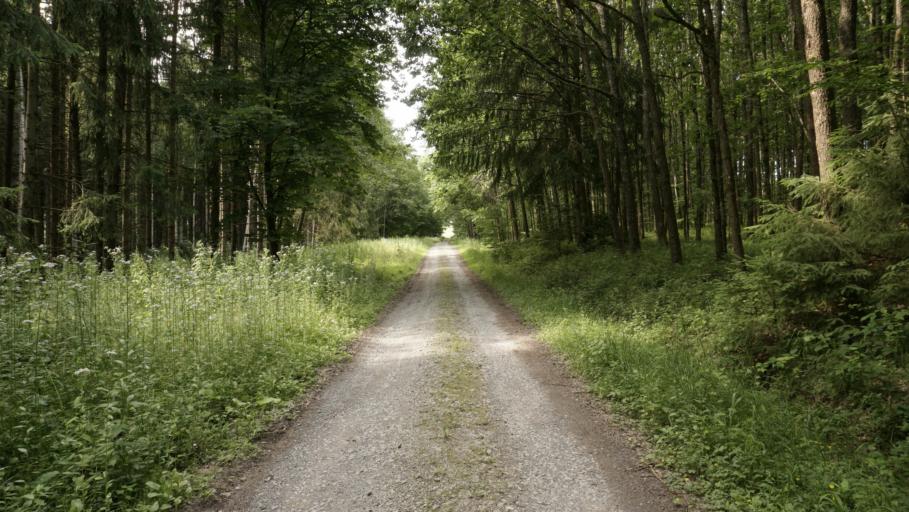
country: DE
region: Baden-Wuerttemberg
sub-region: Karlsruhe Region
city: Mosbach
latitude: 49.3316
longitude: 9.1840
